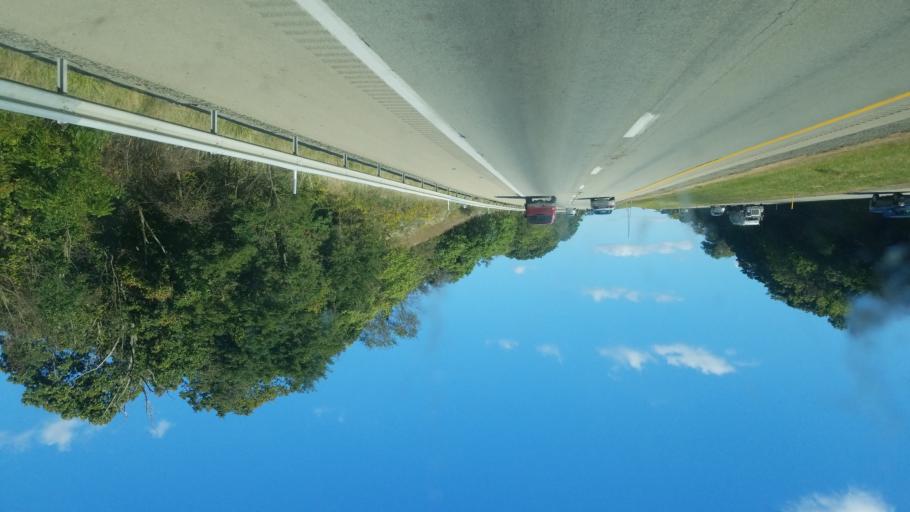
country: US
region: Pennsylvania
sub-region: Greene County
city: Morrisville
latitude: 39.8399
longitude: -80.1125
